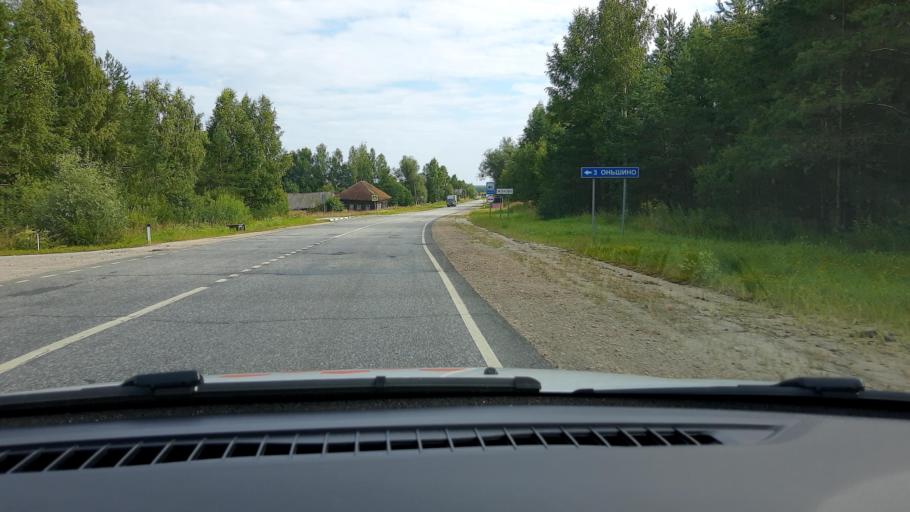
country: RU
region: Nizjnij Novgorod
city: Krasnyye Baki
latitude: 57.0106
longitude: 45.1126
